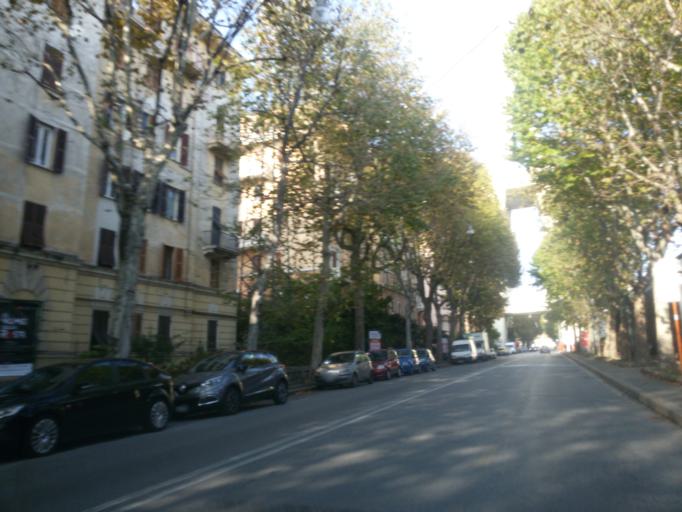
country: IT
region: Liguria
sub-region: Provincia di Genova
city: San Teodoro
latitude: 44.4238
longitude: 8.8900
